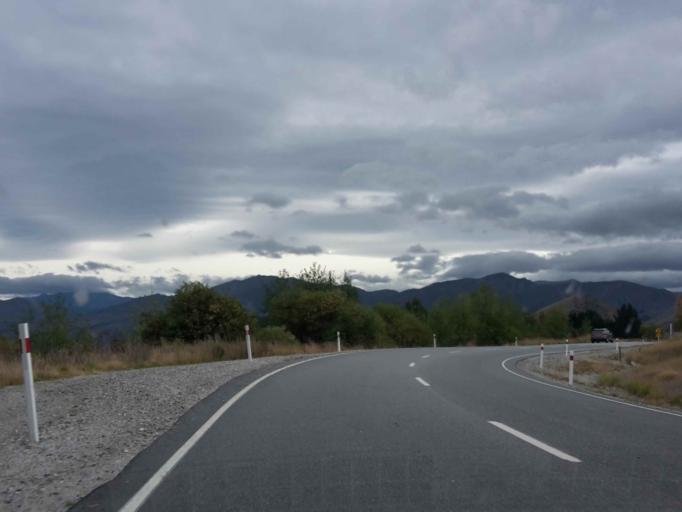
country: NZ
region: Otago
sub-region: Queenstown-Lakes District
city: Arrowtown
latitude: -44.9848
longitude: 168.9027
